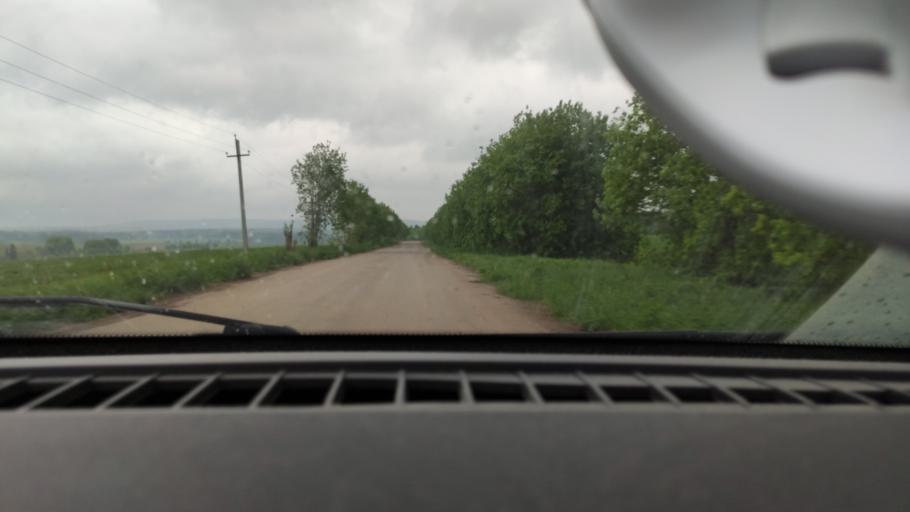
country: RU
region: Perm
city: Gamovo
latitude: 57.8537
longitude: 56.0799
